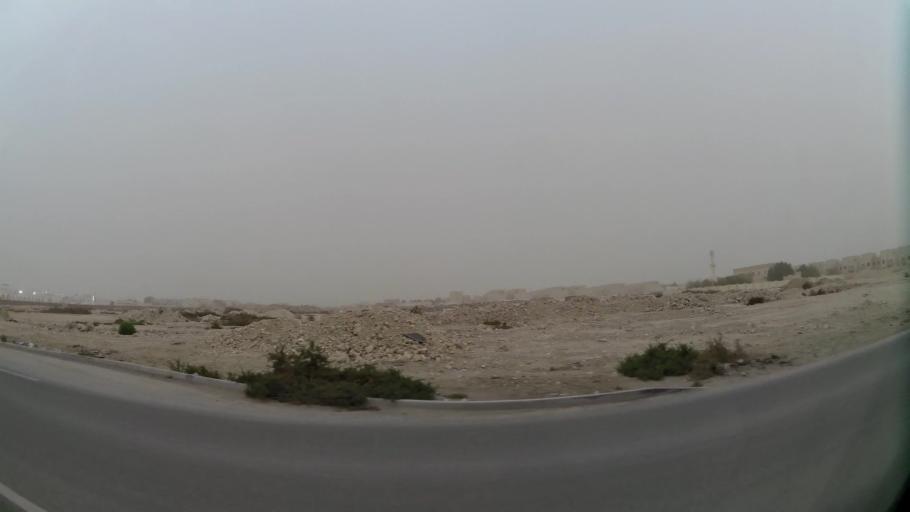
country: QA
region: Baladiyat ad Dawhah
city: Doha
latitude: 25.2438
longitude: 51.4911
